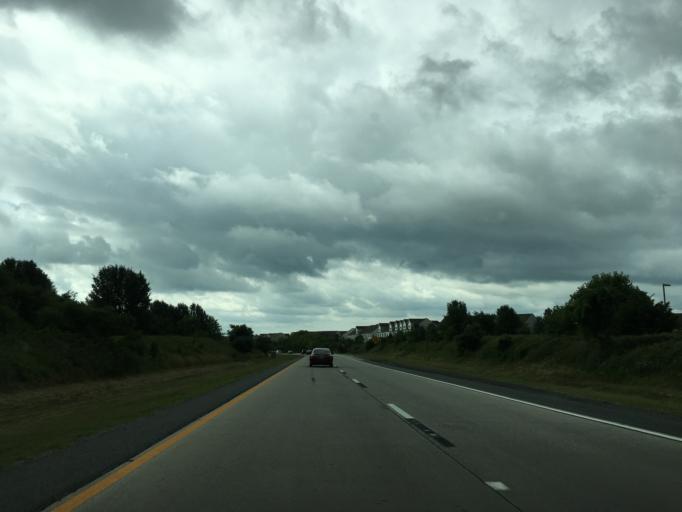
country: US
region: Delaware
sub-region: New Castle County
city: Middletown
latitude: 39.4540
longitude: -75.6765
